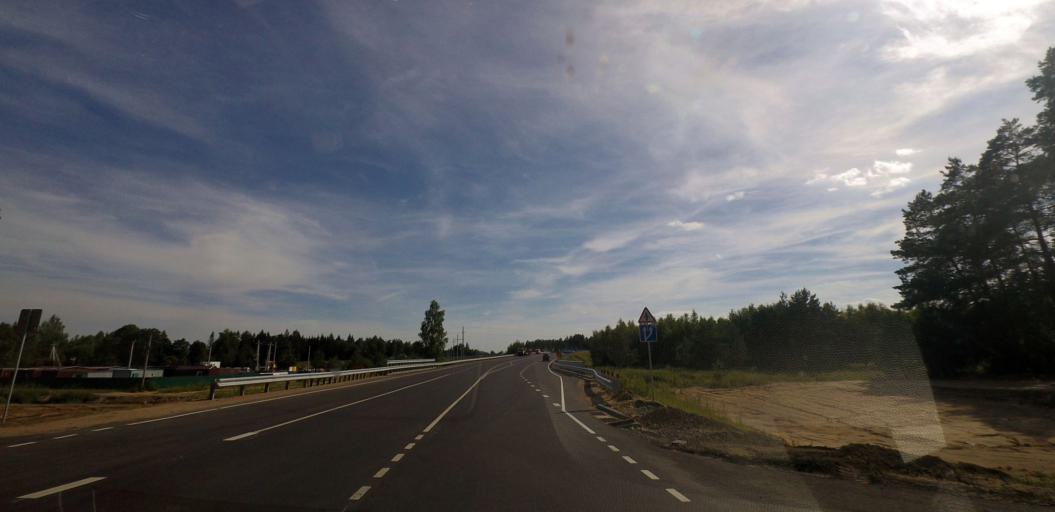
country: BY
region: Grodnenskaya
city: Iwye
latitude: 53.8869
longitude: 25.7427
